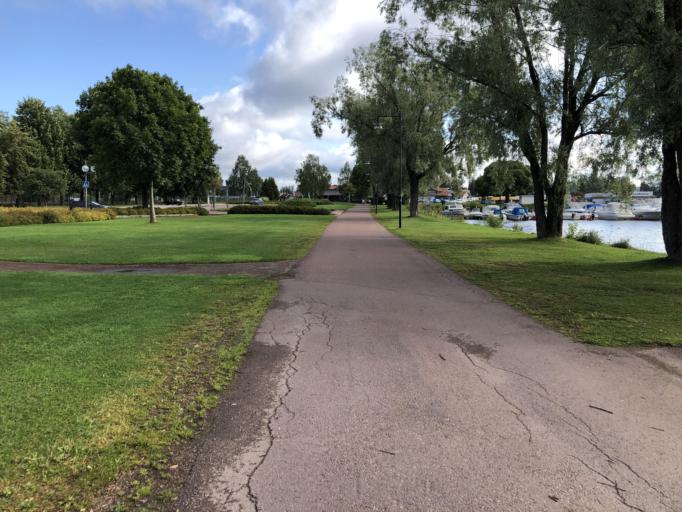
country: SE
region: Dalarna
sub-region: Mora Kommun
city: Mora
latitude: 61.0057
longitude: 14.5455
